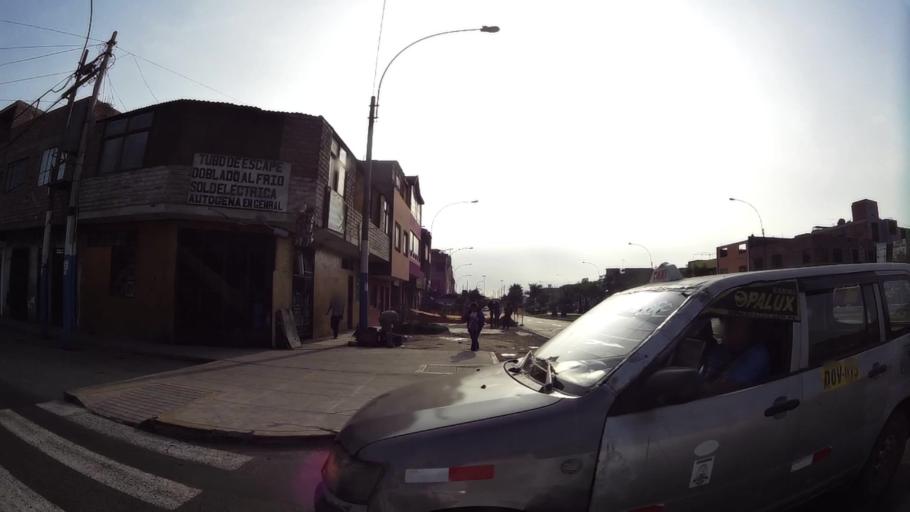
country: PE
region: Lima
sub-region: Lima
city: Independencia
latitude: -12.0276
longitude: -77.0721
